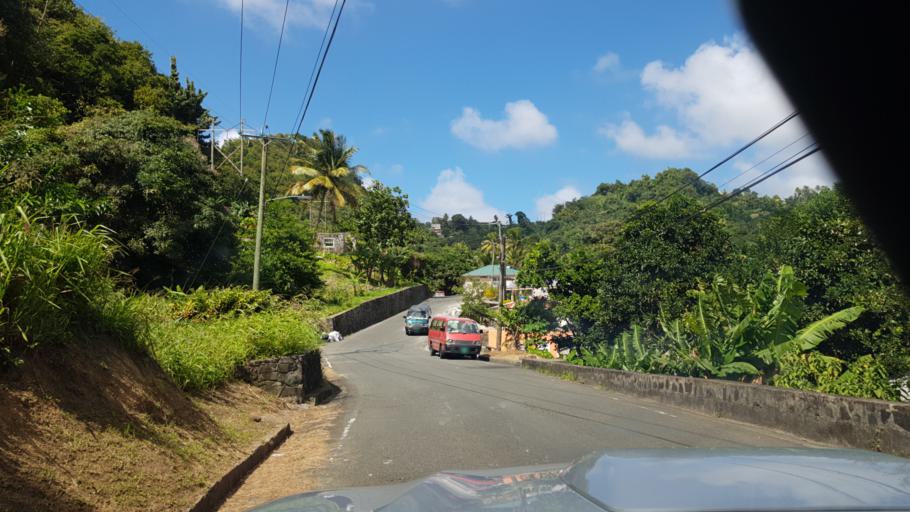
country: LC
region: Castries Quarter
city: Castries
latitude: 13.9856
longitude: -60.9720
